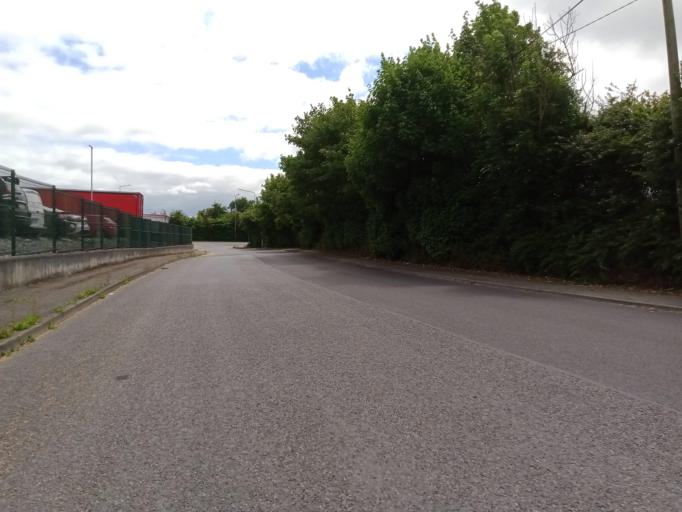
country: IE
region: Leinster
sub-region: Kilkenny
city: Callan
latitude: 52.5550
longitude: -7.3803
